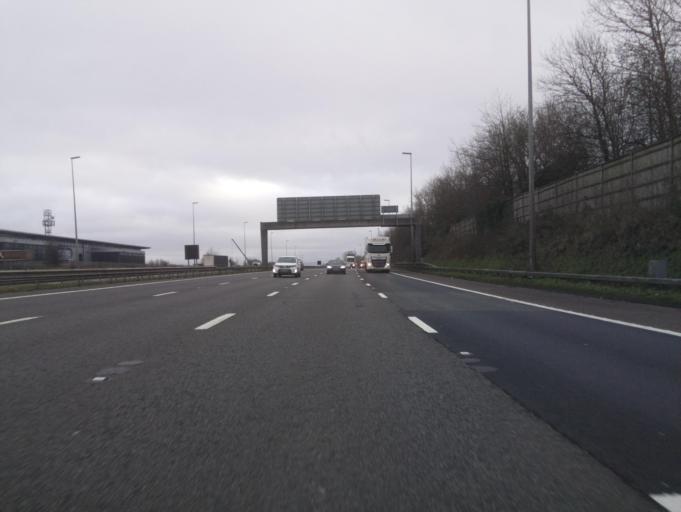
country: GB
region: England
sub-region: Lancashire
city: Goosnargh
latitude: 53.7831
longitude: -2.6504
